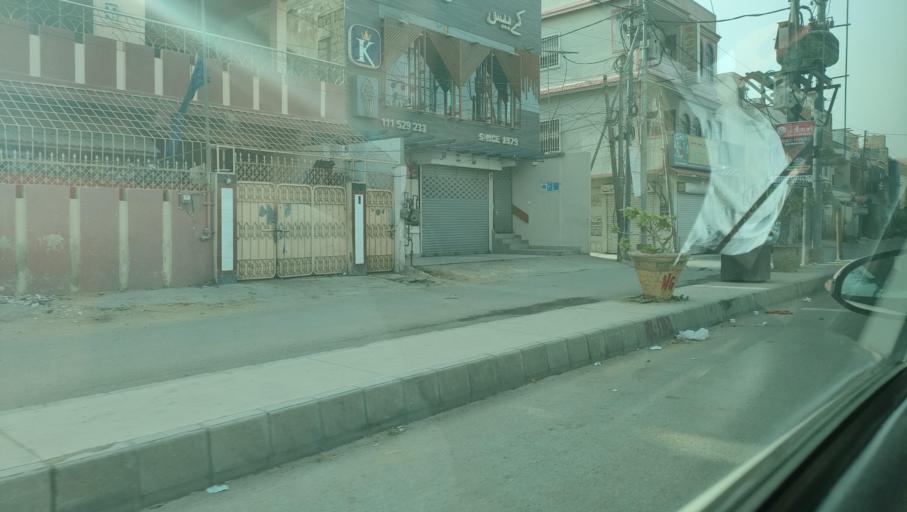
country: PK
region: Sindh
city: Malir Cantonment
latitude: 24.9088
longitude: 67.1838
